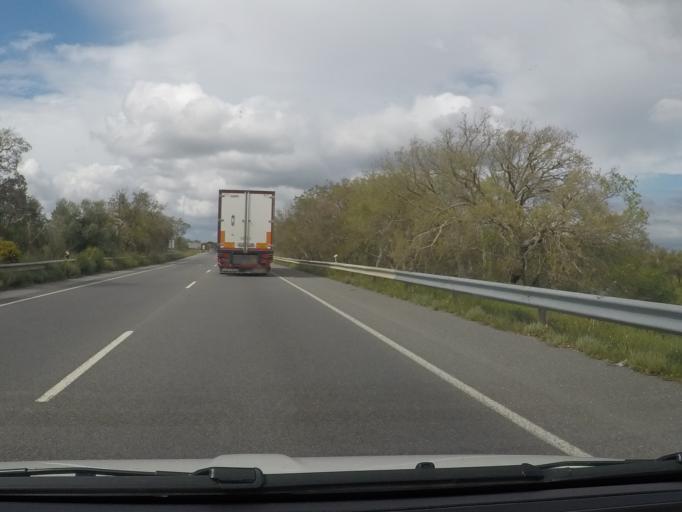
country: PT
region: Setubal
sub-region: Grandola
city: Grandola
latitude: 38.1505
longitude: -8.6497
